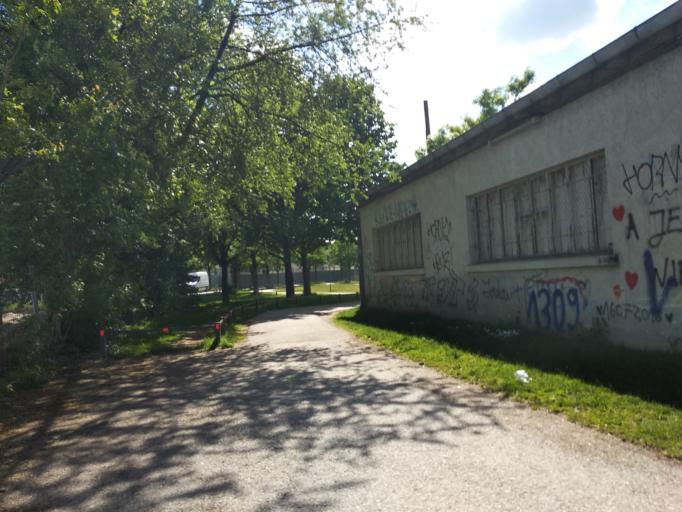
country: DE
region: Bavaria
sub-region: Upper Bavaria
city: Munich
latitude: 48.1621
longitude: 11.5489
